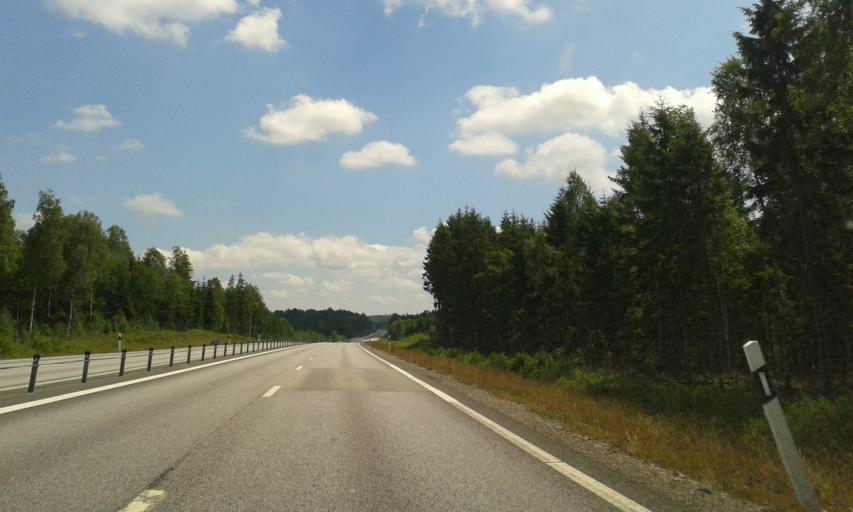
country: SE
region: Kronoberg
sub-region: Vaxjo Kommun
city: Gemla
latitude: 56.9056
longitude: 14.6583
